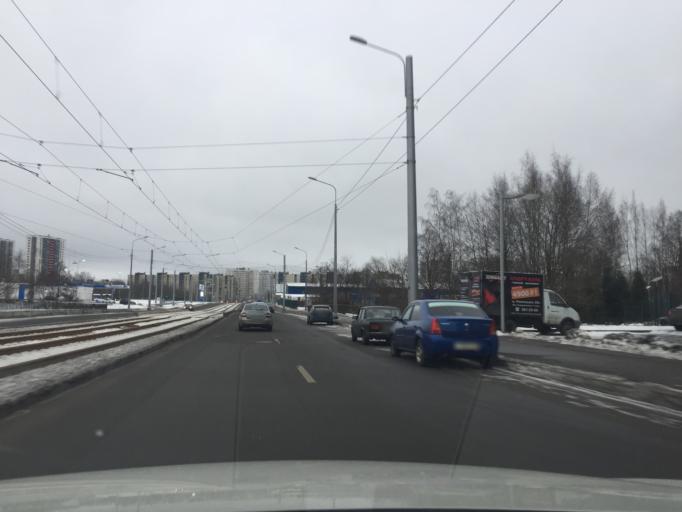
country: RU
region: St.-Petersburg
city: Krasnogvargeisky
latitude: 59.9621
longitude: 30.4673
